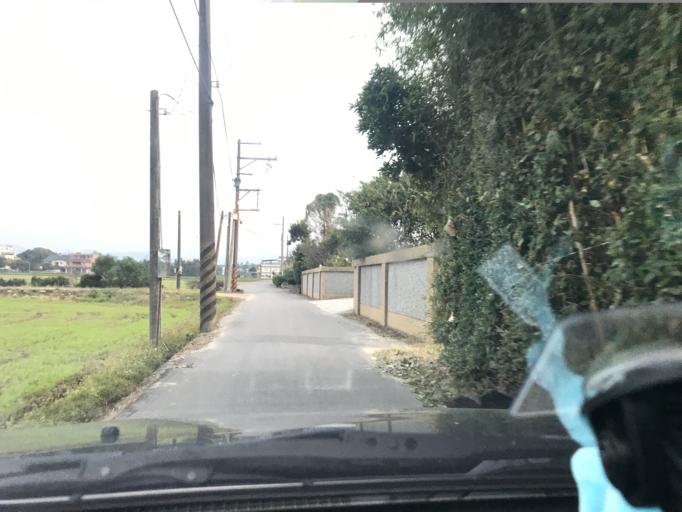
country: TW
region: Taiwan
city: Daxi
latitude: 24.8484
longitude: 121.2102
